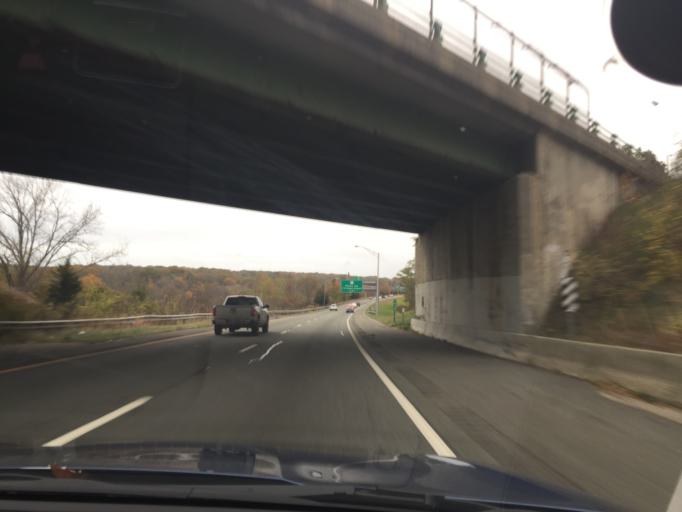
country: US
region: Rhode Island
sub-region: Providence County
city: Cranston
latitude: 41.7661
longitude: -71.4828
